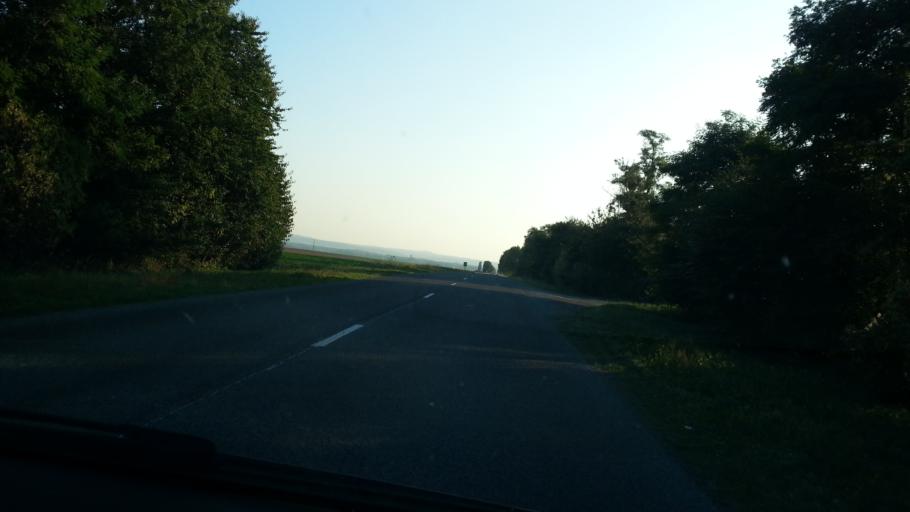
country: FR
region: Picardie
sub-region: Departement de l'Oise
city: Grandfresnoy
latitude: 49.3754
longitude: 2.6172
